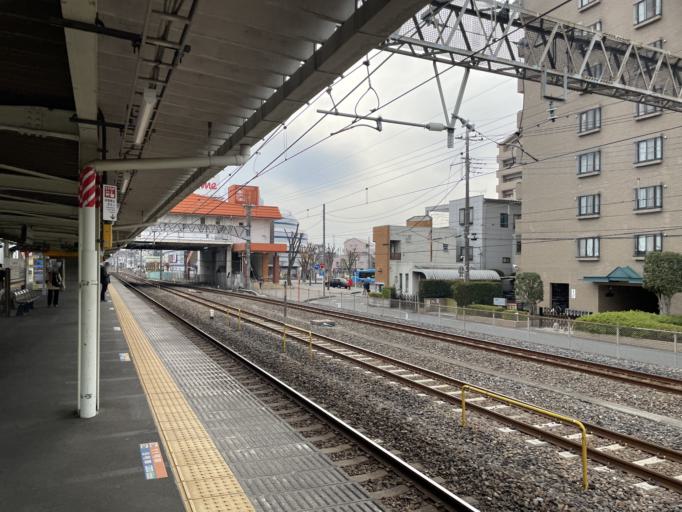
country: JP
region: Saitama
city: Saitama
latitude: 35.9325
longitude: 139.6325
